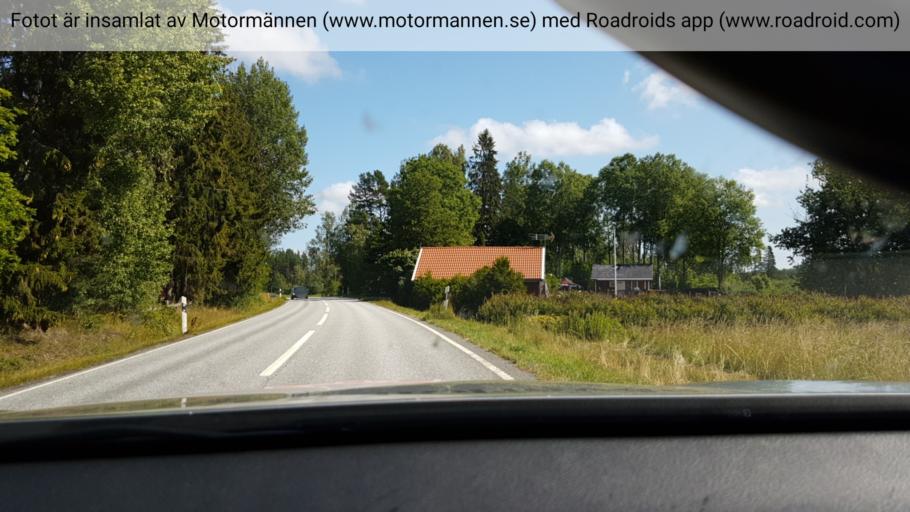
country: SE
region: Stockholm
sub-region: Norrtalje Kommun
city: Hallstavik
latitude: 59.9399
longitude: 18.7441
